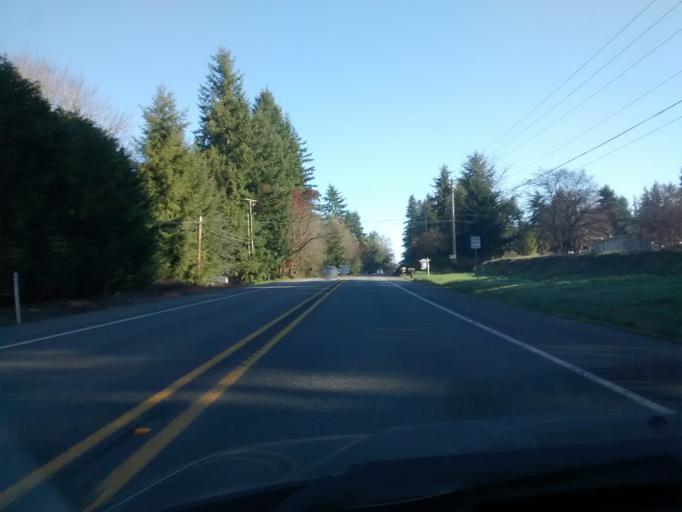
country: US
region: Washington
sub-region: Kitsap County
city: Lofall
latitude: 47.8197
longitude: -122.6420
